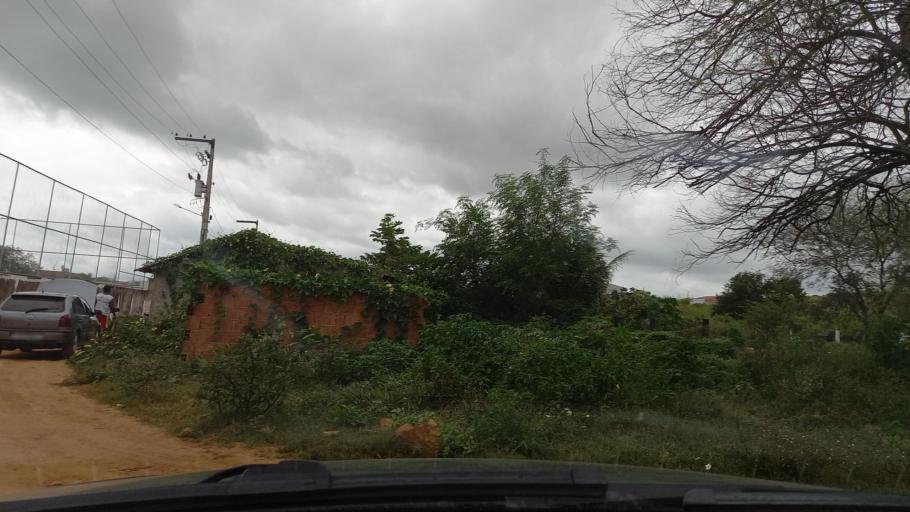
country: BR
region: Sergipe
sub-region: Caninde De Sao Francisco
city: Caninde de Sao Francisco
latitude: -9.6691
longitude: -37.7926
